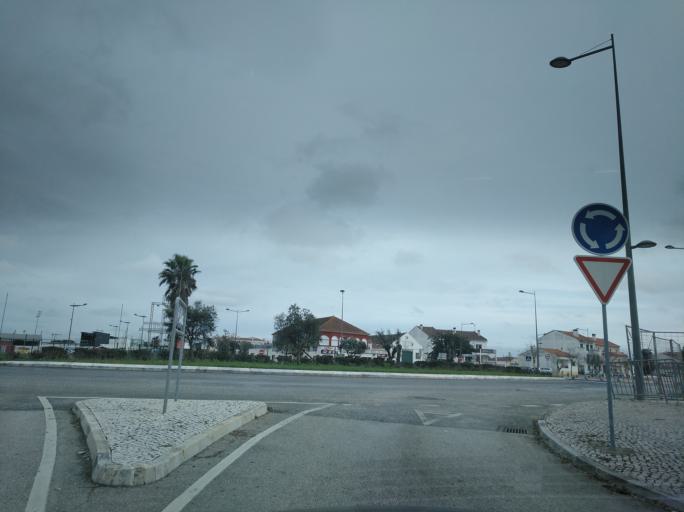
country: PT
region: Setubal
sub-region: Grandola
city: Grandola
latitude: 38.1844
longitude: -8.5684
